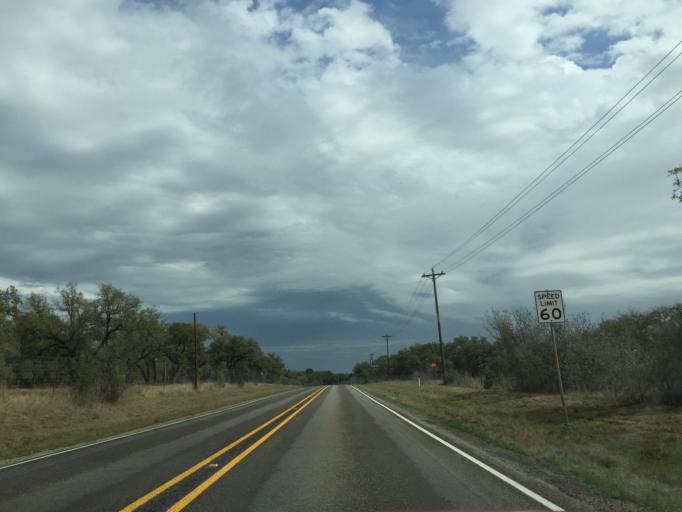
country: US
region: Texas
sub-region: Burnet County
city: Bertram
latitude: 30.6567
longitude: -97.9600
